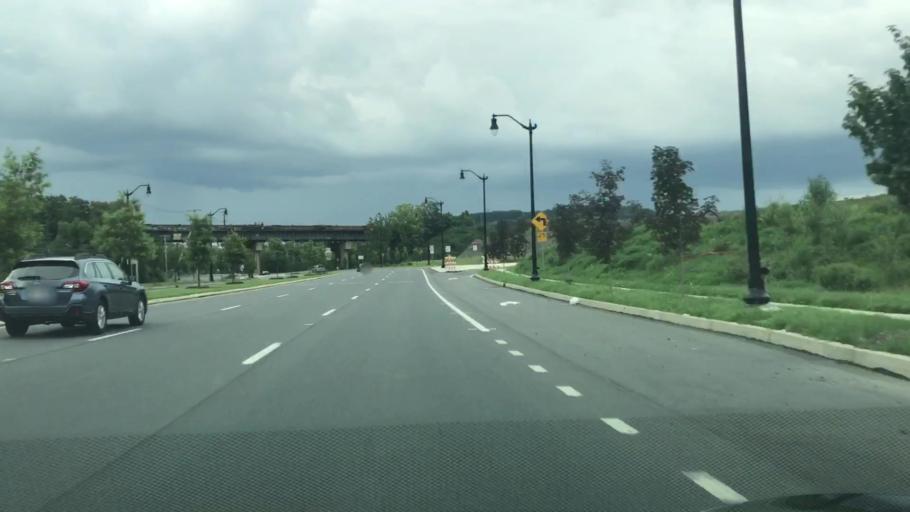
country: US
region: Pennsylvania
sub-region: Northampton County
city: Freemansburg
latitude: 40.6061
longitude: -75.3401
